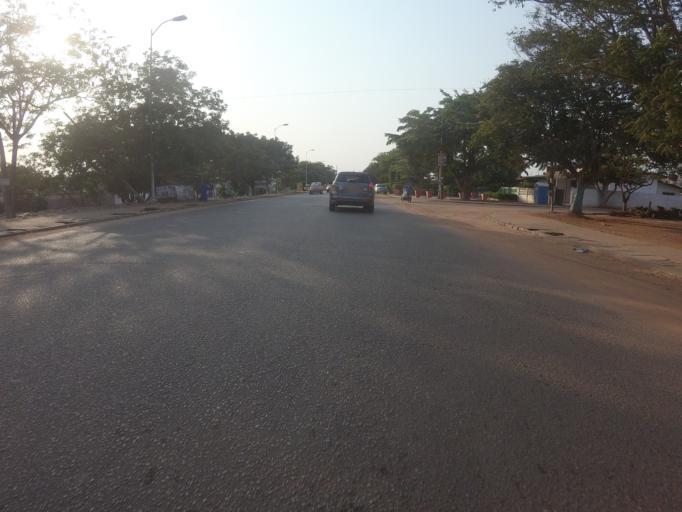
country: GH
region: Greater Accra
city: Nungua
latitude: 5.6225
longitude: -0.0577
